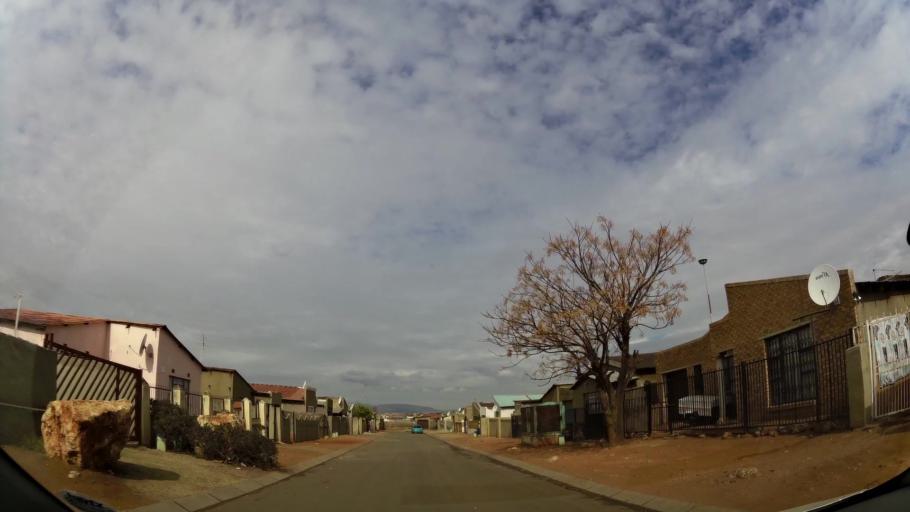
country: ZA
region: Gauteng
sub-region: Ekurhuleni Metropolitan Municipality
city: Germiston
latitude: -26.3796
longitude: 28.1659
